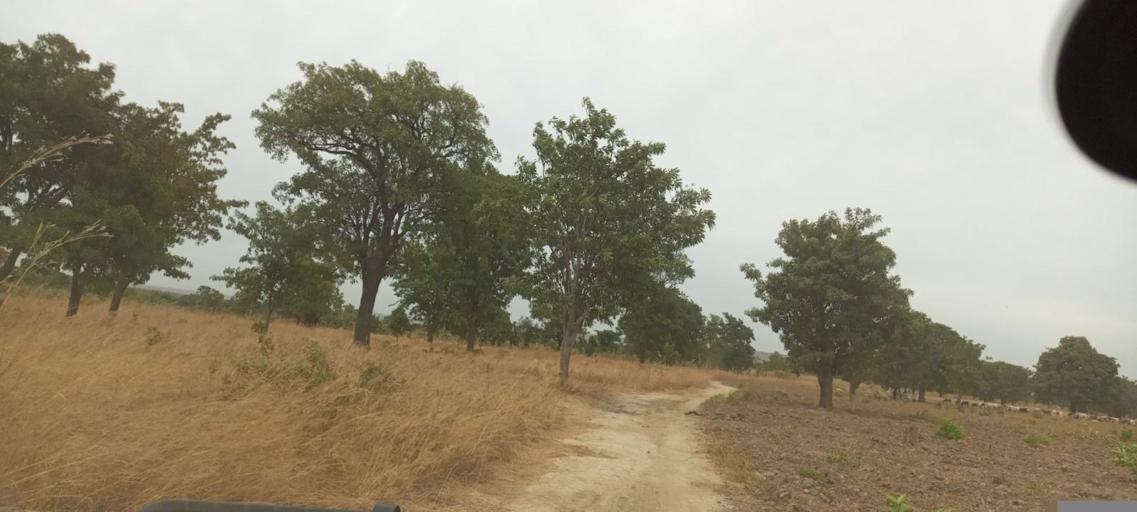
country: ML
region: Koulikoro
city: Kati
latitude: 12.7684
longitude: -8.3798
